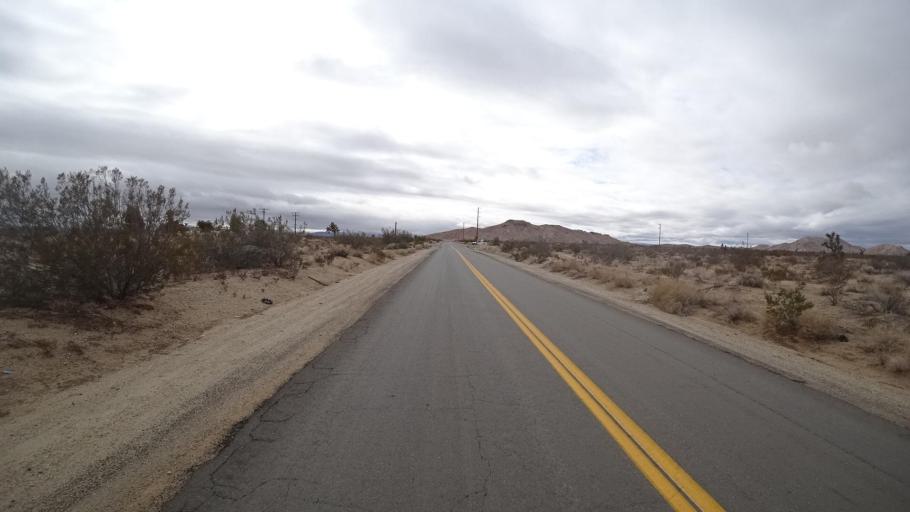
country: US
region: California
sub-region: Kern County
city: Rosamond
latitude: 34.8937
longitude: -118.2201
